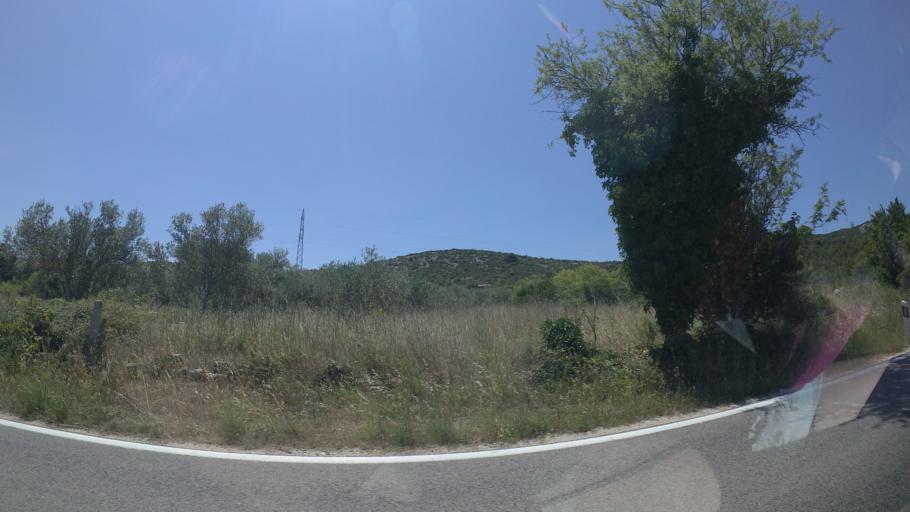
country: HR
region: Sibensko-Kniniska
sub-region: Grad Sibenik
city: Pirovac
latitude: 43.7978
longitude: 15.6783
